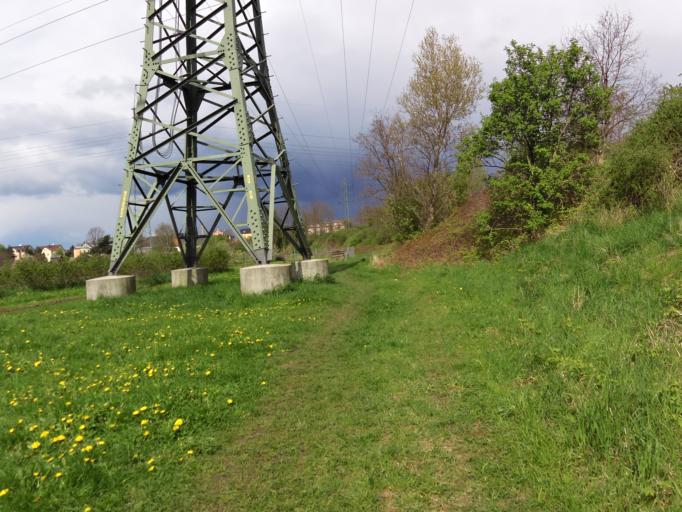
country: DE
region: Saxony
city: Coswig
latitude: 51.1120
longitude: 13.5805
